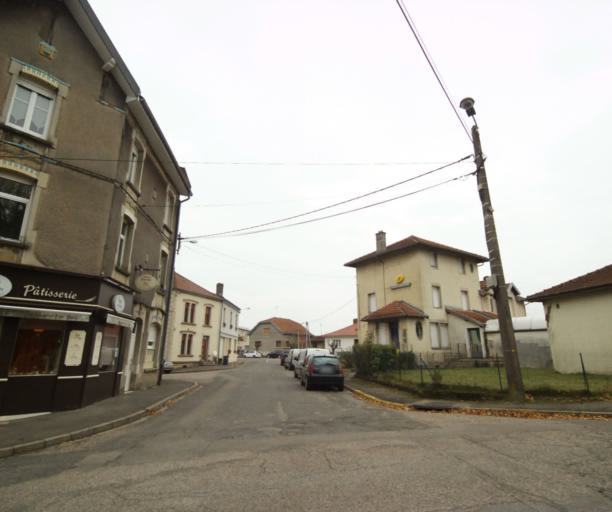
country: FR
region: Lorraine
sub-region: Departement de Meurthe-et-Moselle
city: Mancieulles
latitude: 49.2837
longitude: 5.8943
